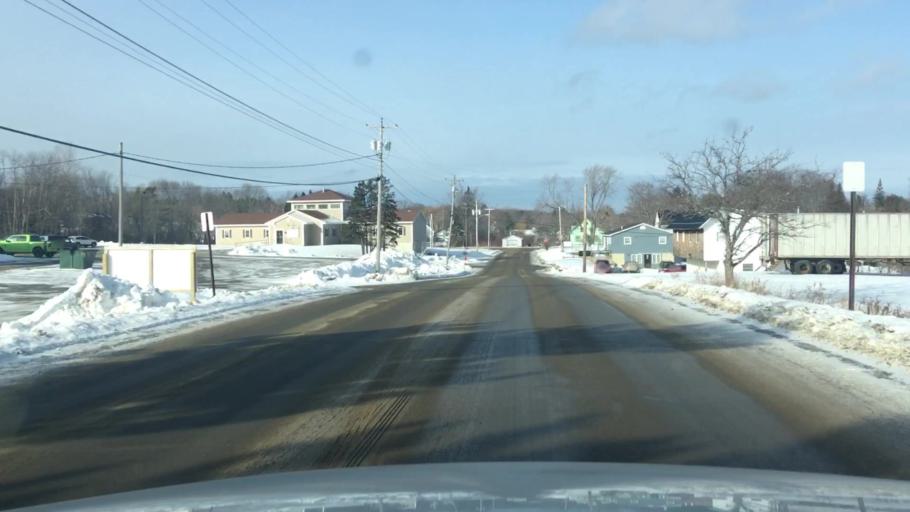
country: US
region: Maine
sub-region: Washington County
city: Calais
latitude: 45.1800
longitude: -67.2679
